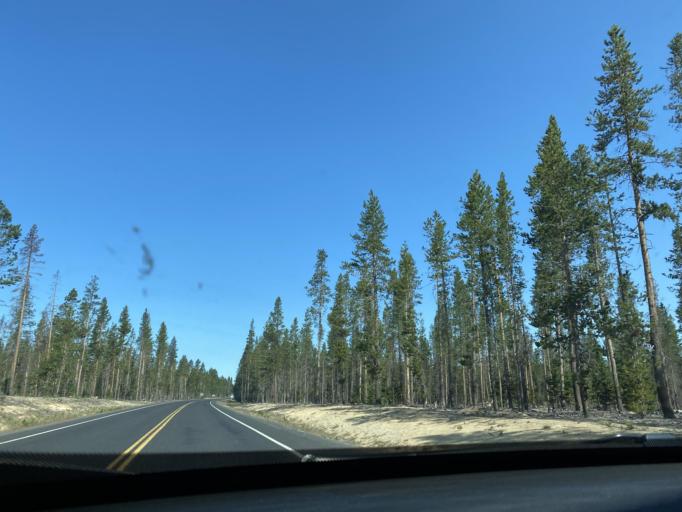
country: US
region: Oregon
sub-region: Deschutes County
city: Three Rivers
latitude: 43.7081
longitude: -121.2704
